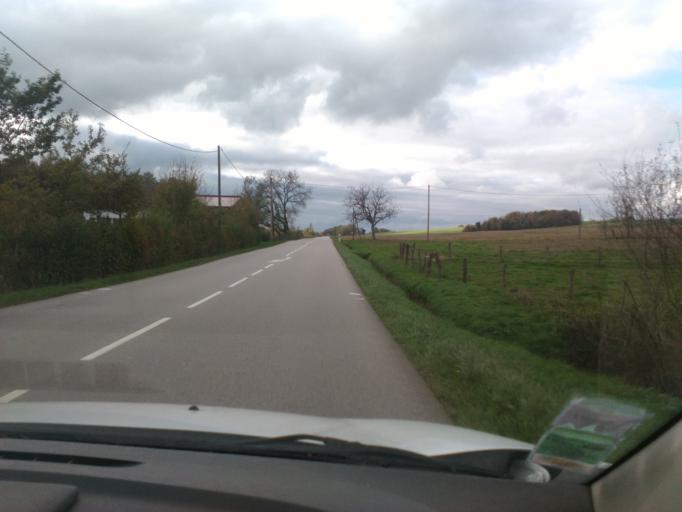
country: FR
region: Lorraine
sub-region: Departement des Vosges
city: Jeanmenil
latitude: 48.3523
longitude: 6.7136
